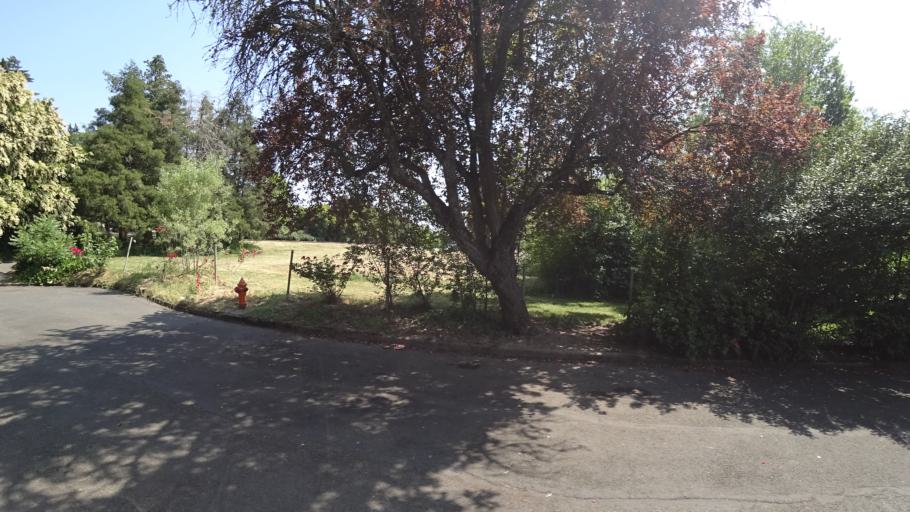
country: US
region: Oregon
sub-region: Multnomah County
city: Lents
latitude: 45.5086
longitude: -122.5981
